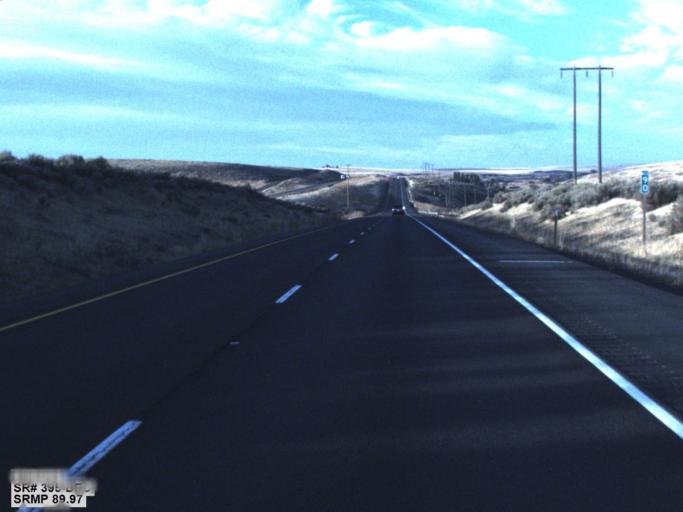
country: US
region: Washington
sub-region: Adams County
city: Ritzville
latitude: 47.0432
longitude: -118.4481
